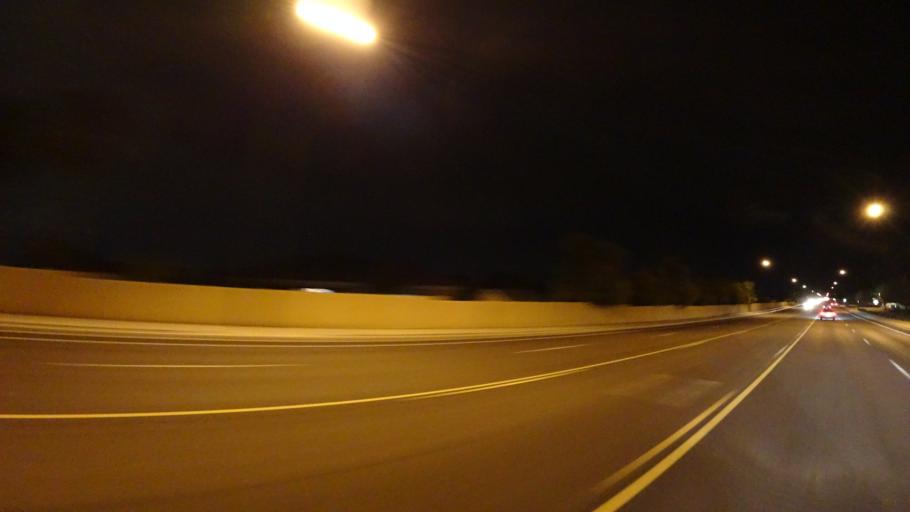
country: US
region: Arizona
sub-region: Maricopa County
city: Queen Creek
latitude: 33.2338
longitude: -111.7356
